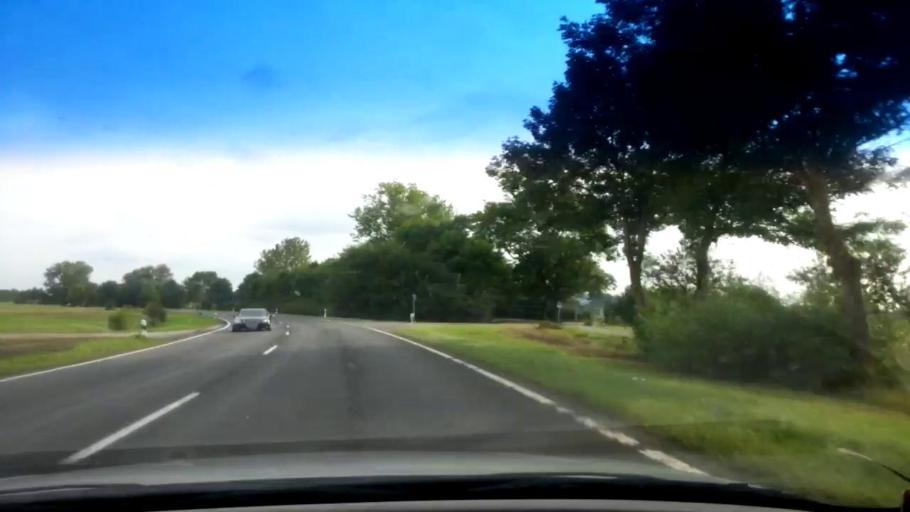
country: DE
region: Bavaria
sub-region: Upper Franconia
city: Rattelsdorf
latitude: 49.9950
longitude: 10.8823
